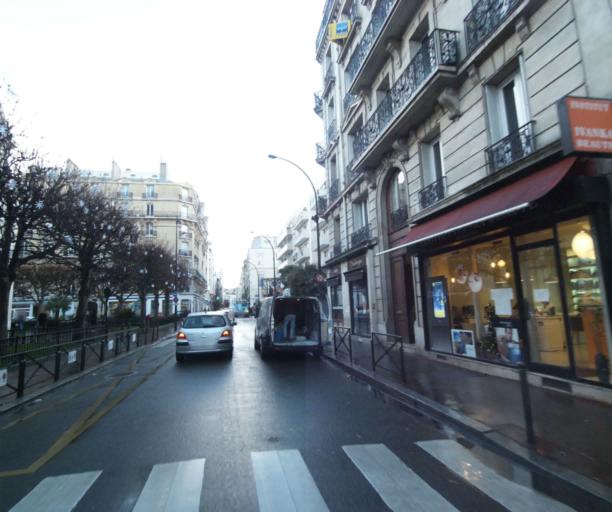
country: FR
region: Ile-de-France
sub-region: Departement des Hauts-de-Seine
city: Levallois-Perret
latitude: 48.8944
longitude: 2.2894
